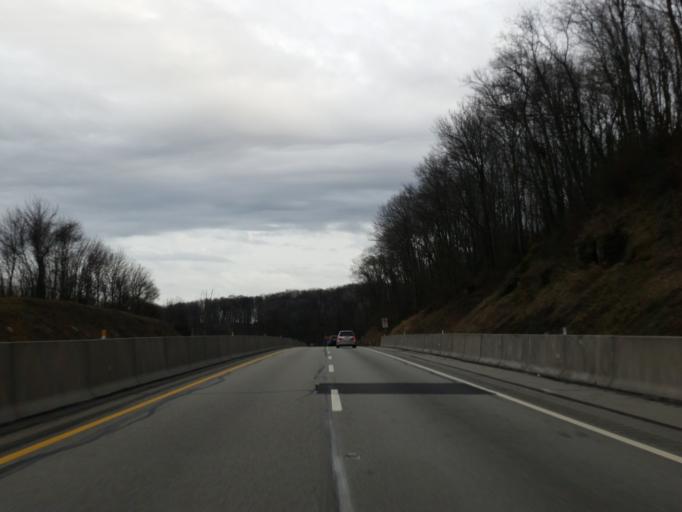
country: US
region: Pennsylvania
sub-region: Somerset County
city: Somerset
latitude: 40.0430
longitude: -79.1176
